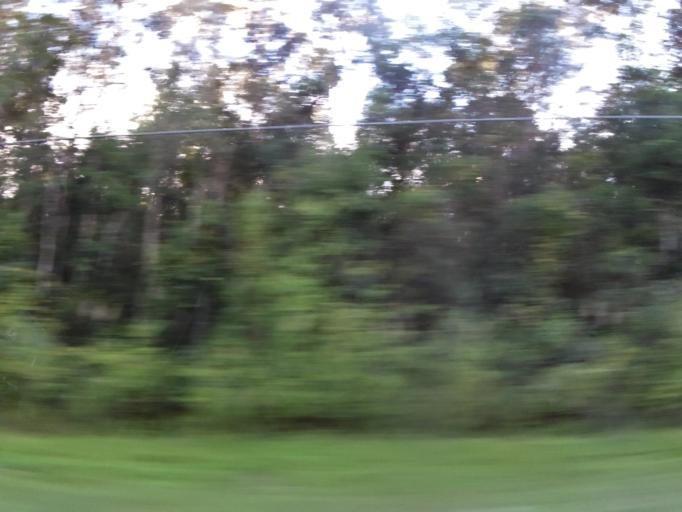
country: US
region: Georgia
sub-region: Lowndes County
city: Valdosta
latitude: 30.7798
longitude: -83.1574
